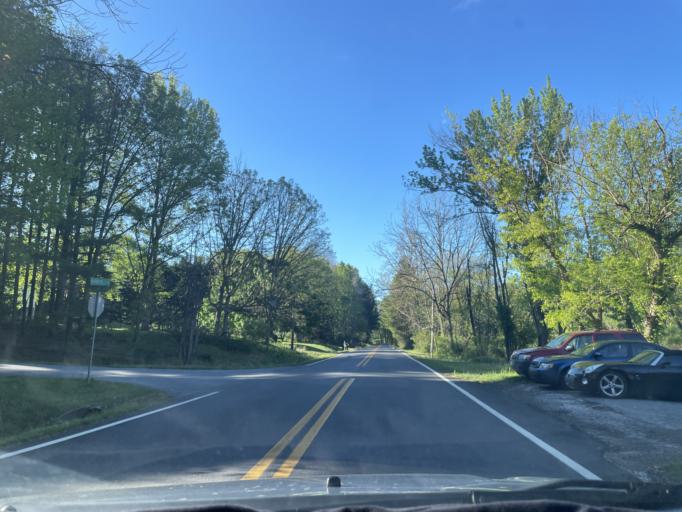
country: US
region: Maryland
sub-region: Carroll County
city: Mount Airy
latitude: 39.4152
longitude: -77.1377
